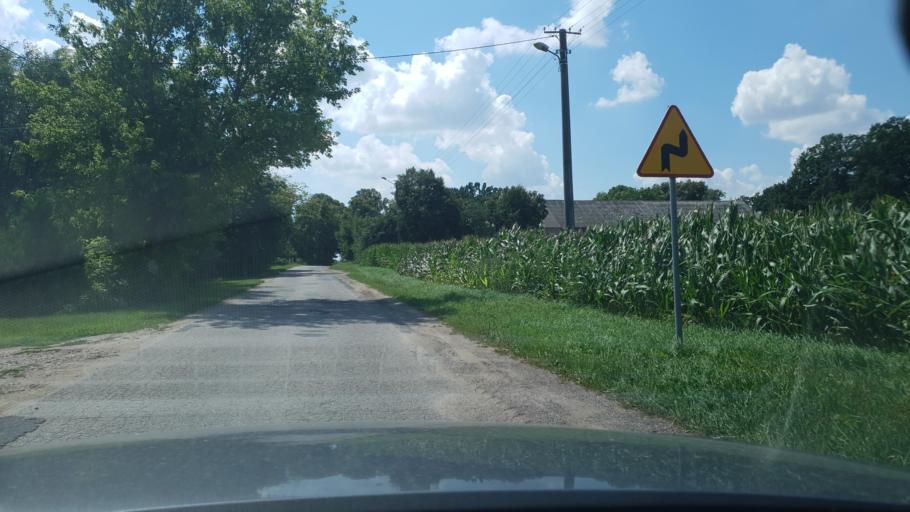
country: PL
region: Kujawsko-Pomorskie
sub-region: Powiat wabrzeski
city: Pluznica
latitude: 53.2960
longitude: 18.8031
